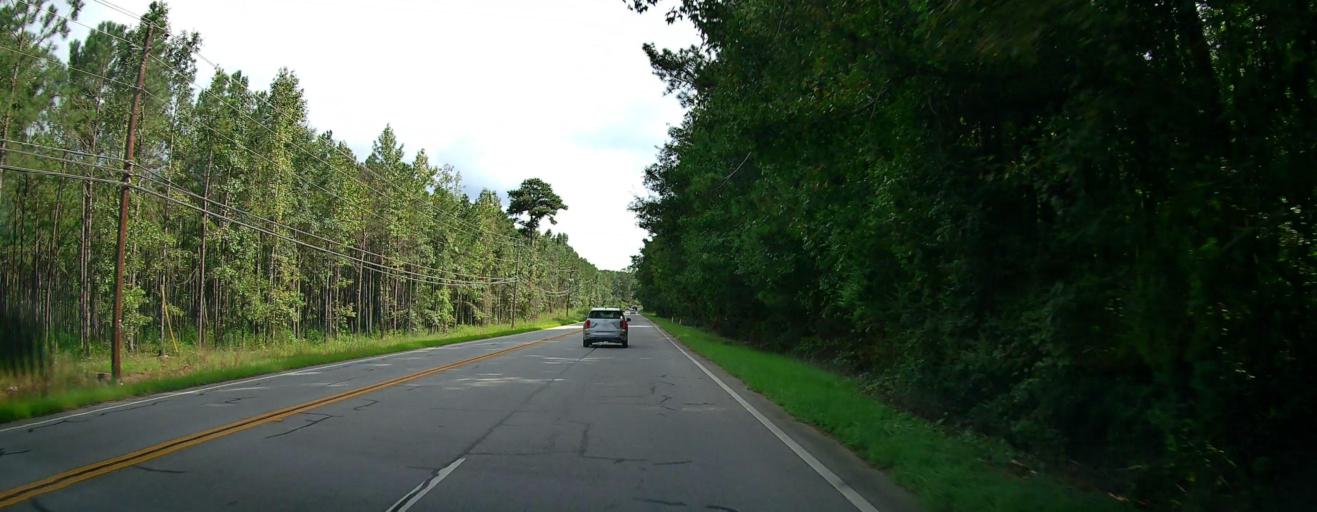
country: US
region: Alabama
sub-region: Russell County
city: Phenix City
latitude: 32.5961
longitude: -84.9090
